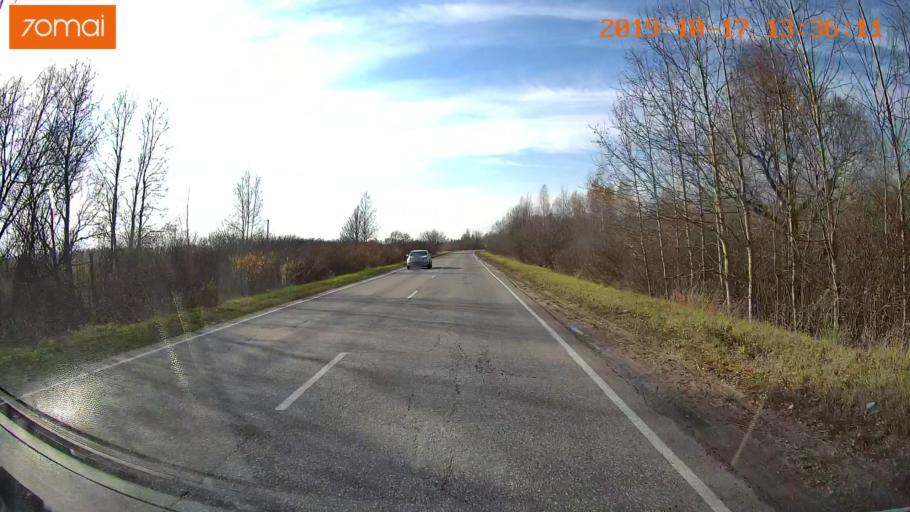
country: RU
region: Vladimir
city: Velikodvorskiy
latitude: 55.1400
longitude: 40.6703
